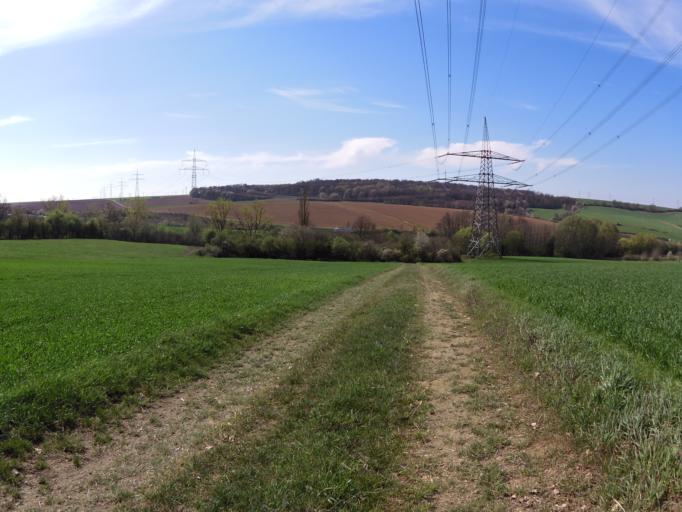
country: DE
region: Bavaria
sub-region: Regierungsbezirk Unterfranken
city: Rottendorf
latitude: 49.7852
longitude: 10.0493
